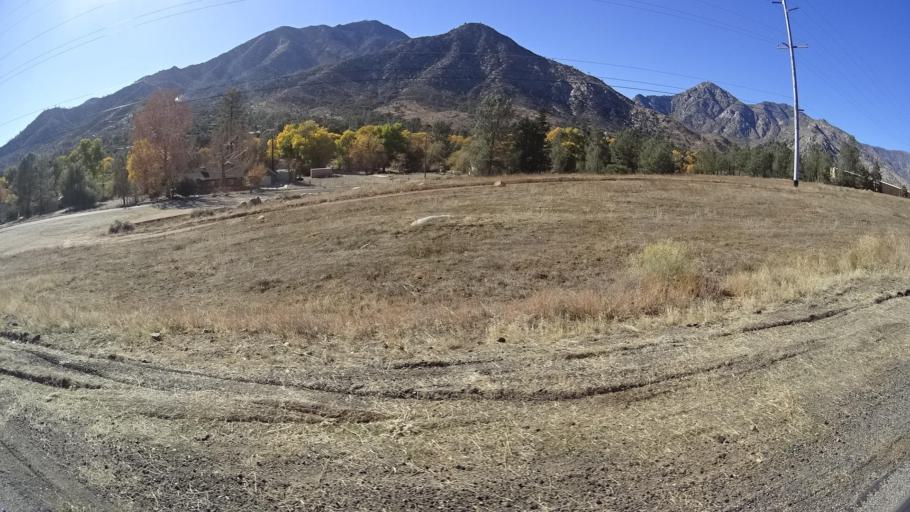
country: US
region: California
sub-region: Kern County
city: Kernville
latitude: 35.7710
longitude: -118.4303
